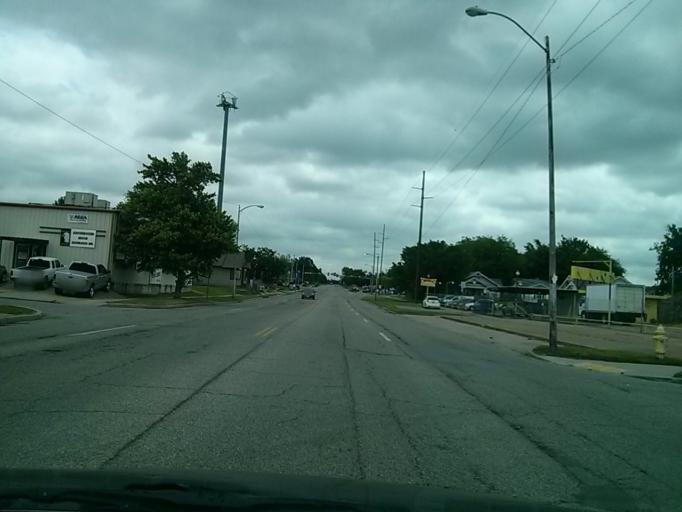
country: US
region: Oklahoma
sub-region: Tulsa County
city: Tulsa
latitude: 36.1566
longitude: -95.9612
